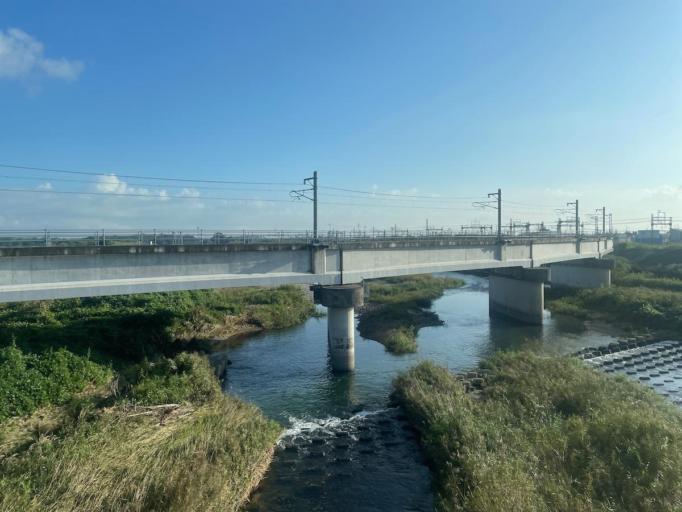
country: JP
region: Mie
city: Hisai-motomachi
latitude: 34.6393
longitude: 136.4744
